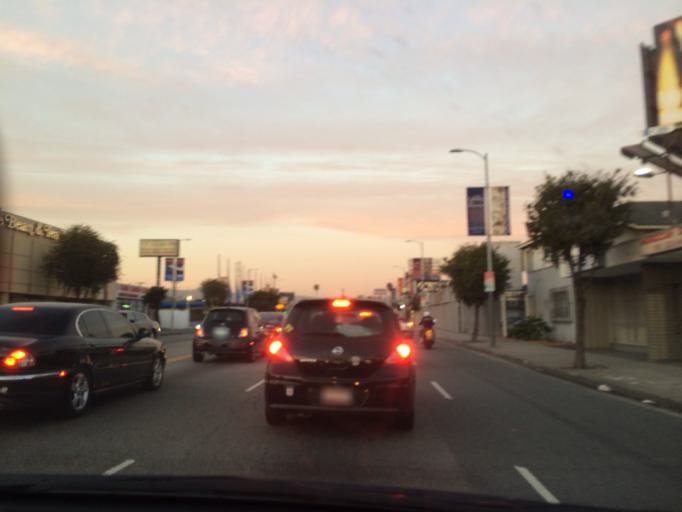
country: US
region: California
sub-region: Los Angeles County
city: Culver City
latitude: 34.0410
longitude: -118.3767
